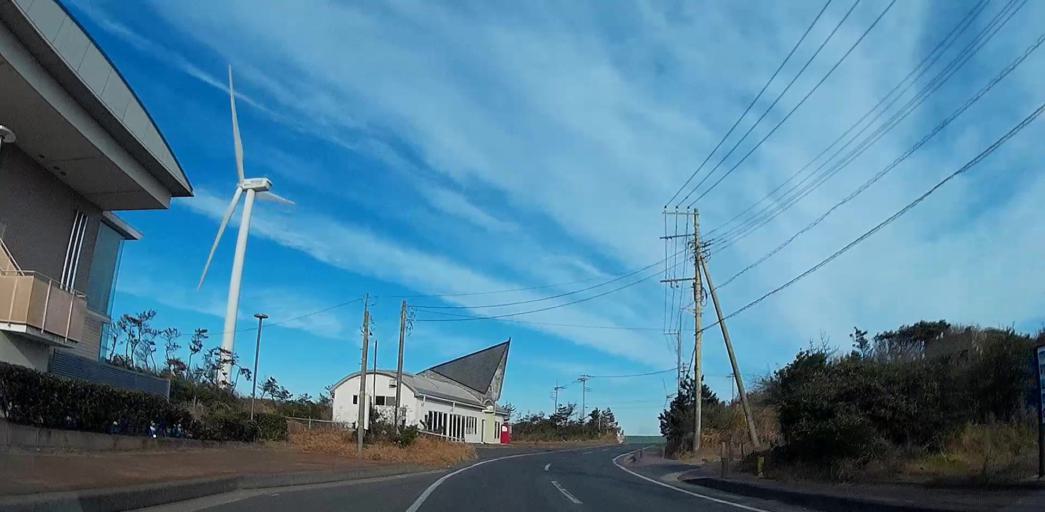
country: JP
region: Chiba
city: Hasaki
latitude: 35.7516
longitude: 140.8306
